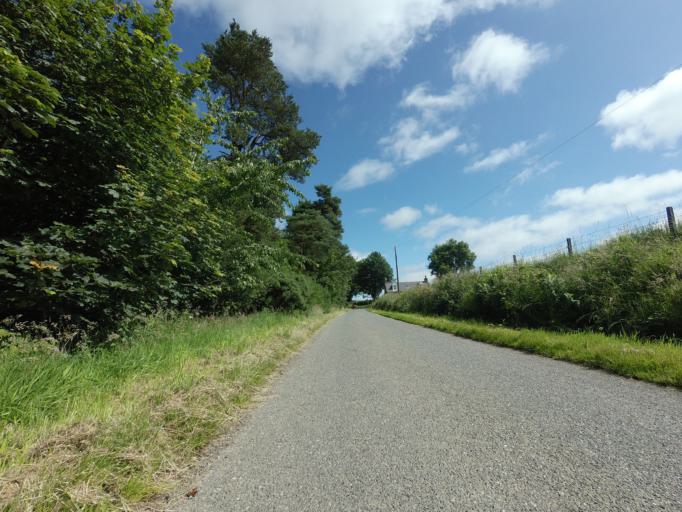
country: GB
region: Scotland
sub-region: Aberdeenshire
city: Turriff
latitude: 57.5843
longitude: -2.5056
